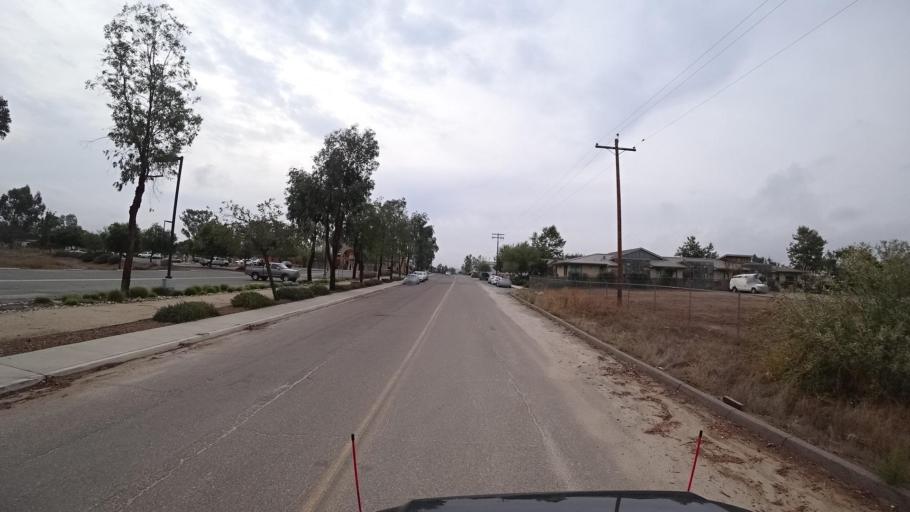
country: US
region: California
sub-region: San Diego County
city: Ramona
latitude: 33.0407
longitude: -116.8743
